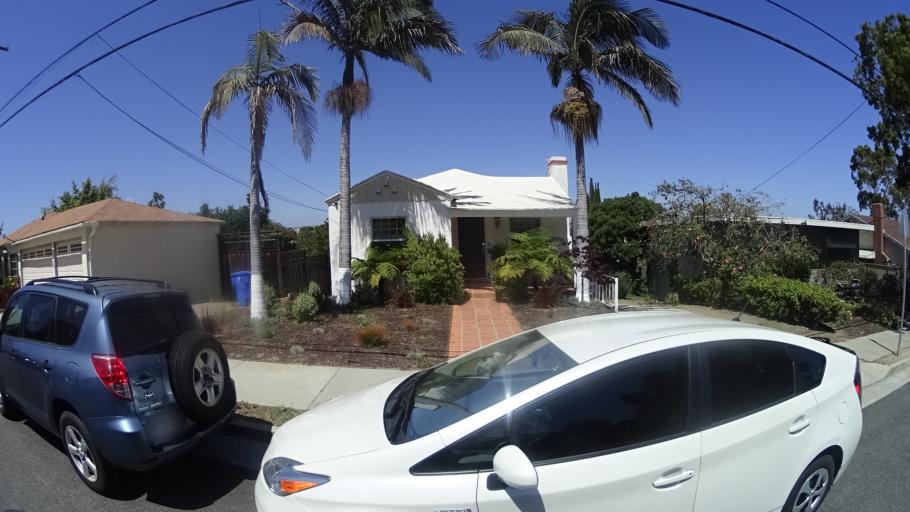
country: US
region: California
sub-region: Los Angeles County
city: Santa Monica
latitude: 34.0068
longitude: -118.4789
